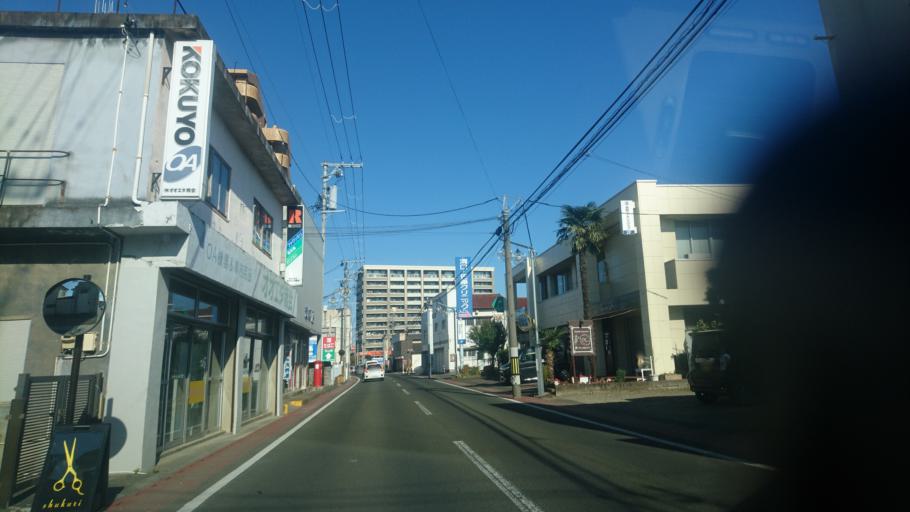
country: JP
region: Miyagi
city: Iwanuma
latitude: 38.1687
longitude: 140.8854
